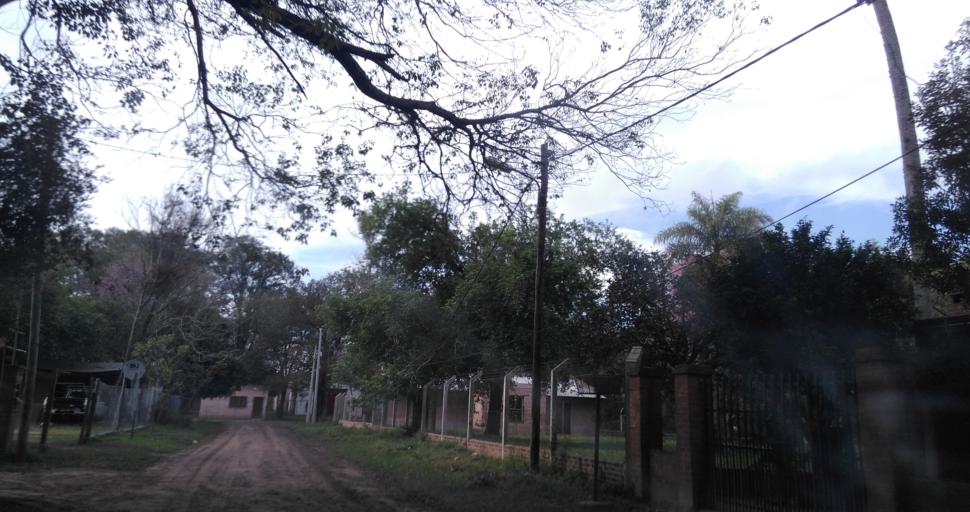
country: AR
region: Chaco
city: Colonia Benitez
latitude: -27.3325
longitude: -58.9547
